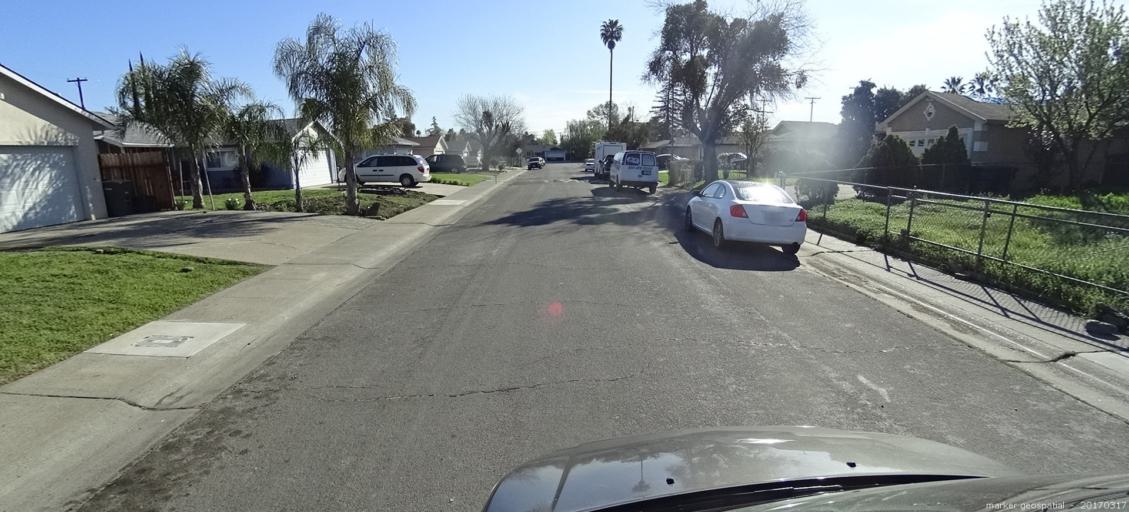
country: US
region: California
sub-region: Sacramento County
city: Parkway
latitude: 38.4827
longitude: -121.5005
